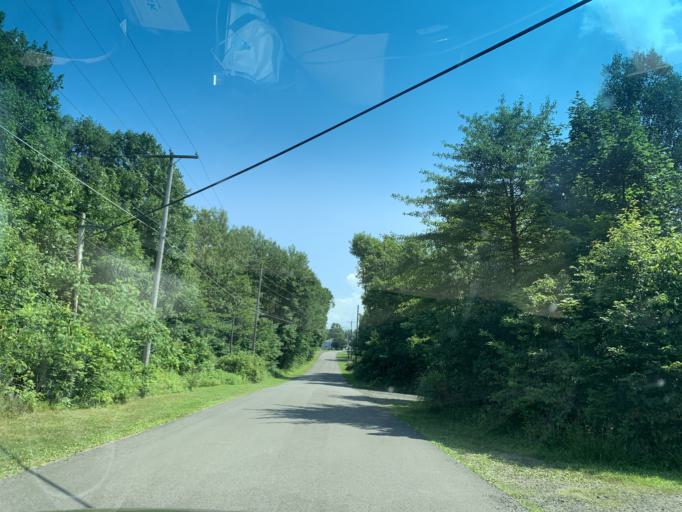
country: US
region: Pennsylvania
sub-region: Schuylkill County
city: Ashland
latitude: 40.8170
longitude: -76.3387
